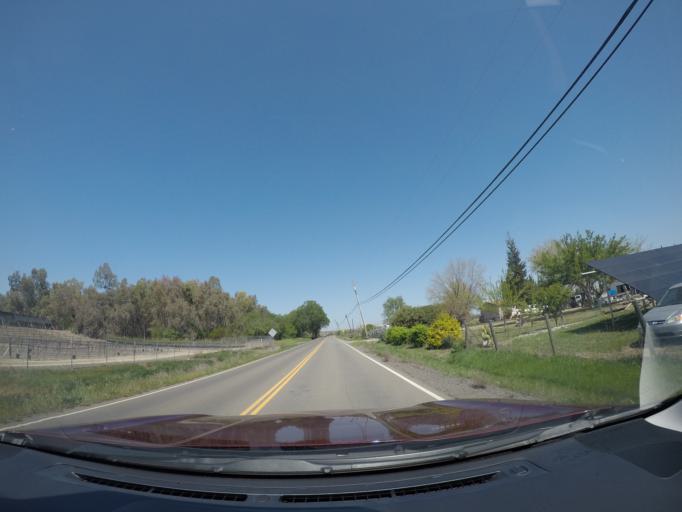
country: US
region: California
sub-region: Yolo County
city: Winters
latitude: 38.4910
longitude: -121.9499
